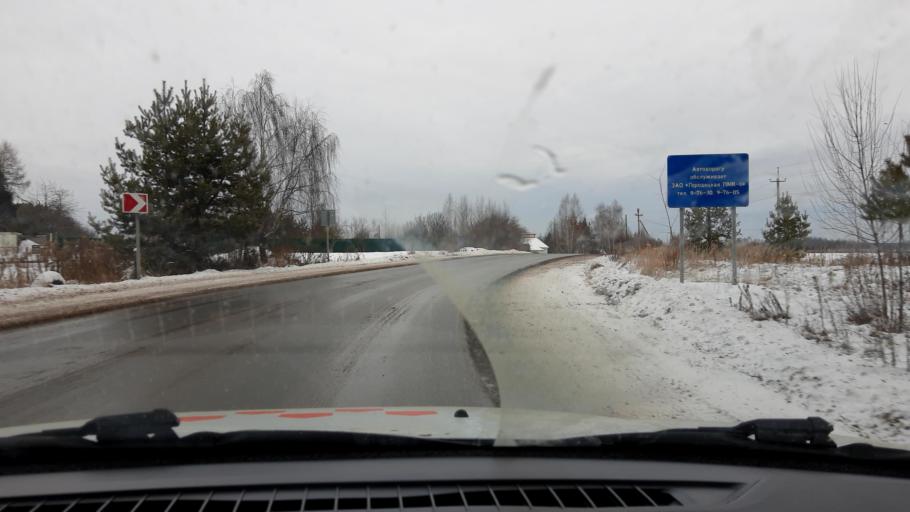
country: RU
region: Nizjnij Novgorod
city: Neklyudovo
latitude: 56.4453
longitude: 43.8992
